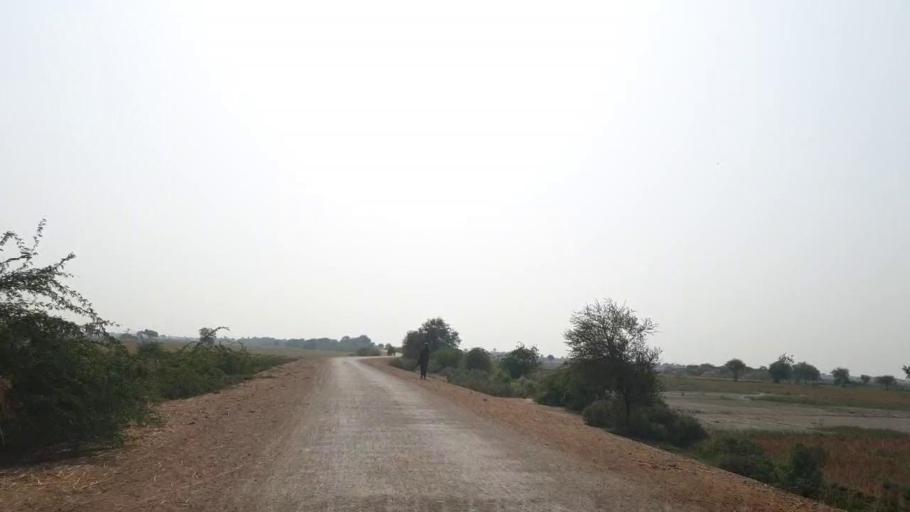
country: PK
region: Sindh
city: Matli
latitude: 24.9711
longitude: 68.5863
